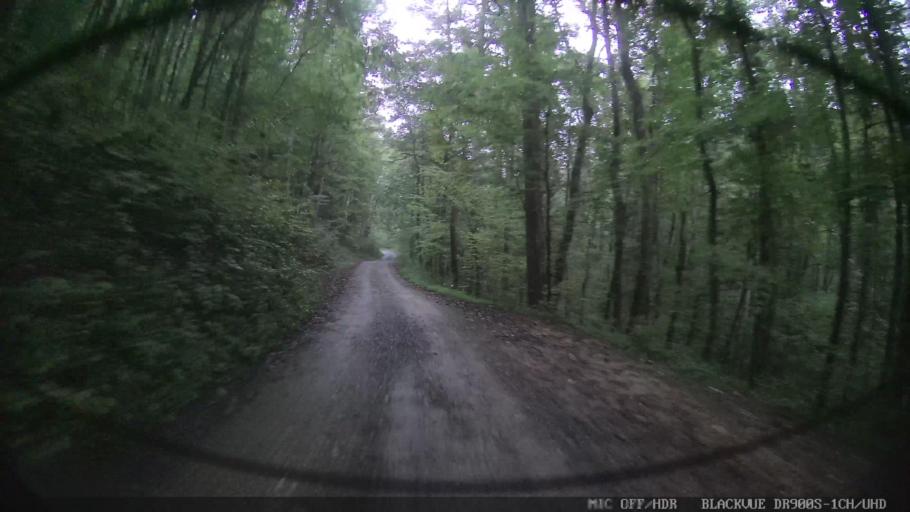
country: US
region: Georgia
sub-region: Gilmer County
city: Ellijay
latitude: 34.8085
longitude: -84.5579
